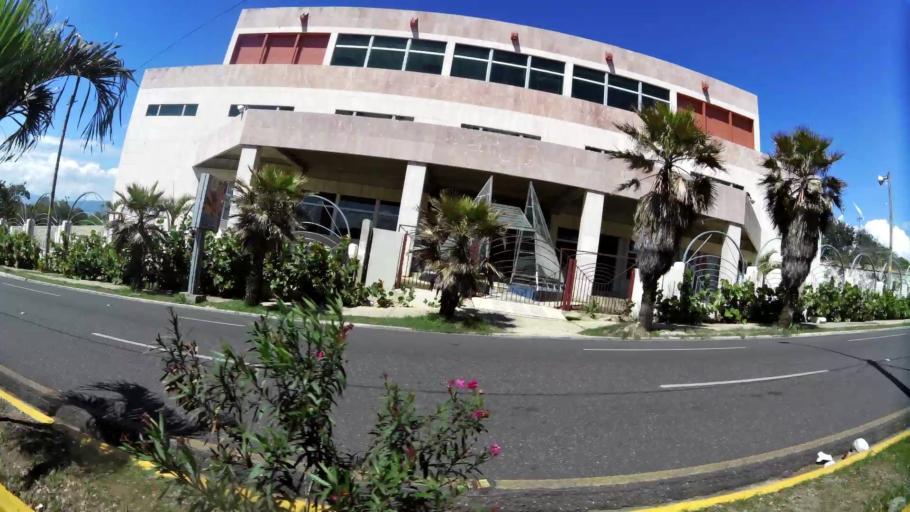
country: DO
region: Santiago
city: Santiago de los Caballeros
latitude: 19.4527
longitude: -70.6947
